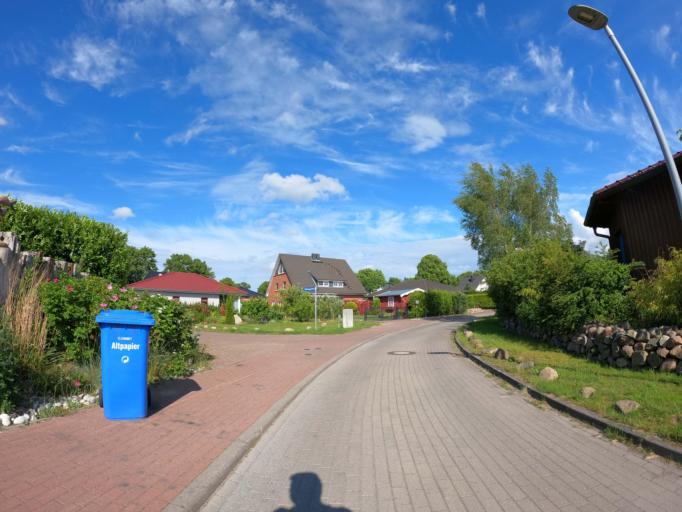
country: DE
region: Mecklenburg-Vorpommern
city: Kramerhof
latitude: 54.3387
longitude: 13.0375
